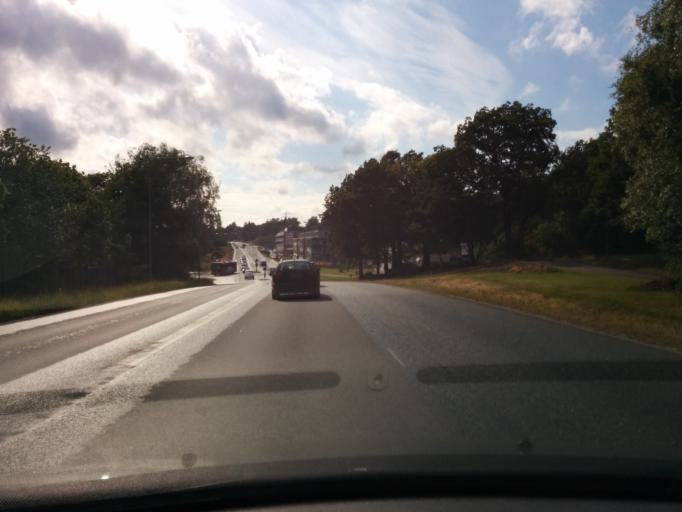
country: SE
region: Stockholm
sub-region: Sollentuna Kommun
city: Sollentuna
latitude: 59.4455
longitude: 17.9584
